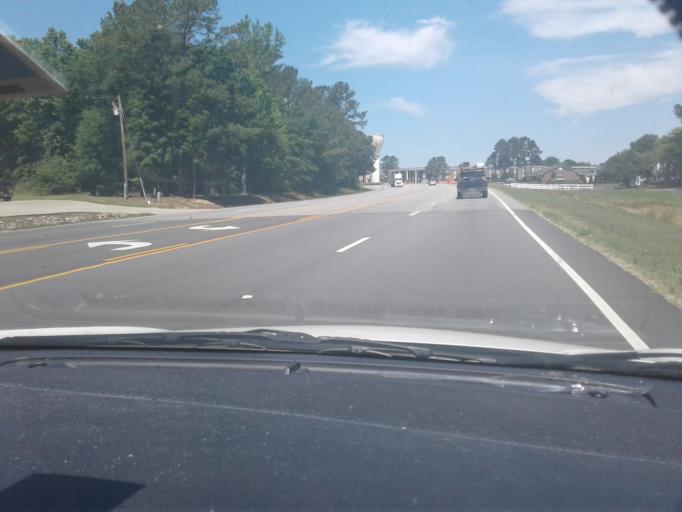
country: US
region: North Carolina
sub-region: Harnett County
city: Buies Creek
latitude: 35.4027
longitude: -78.7374
